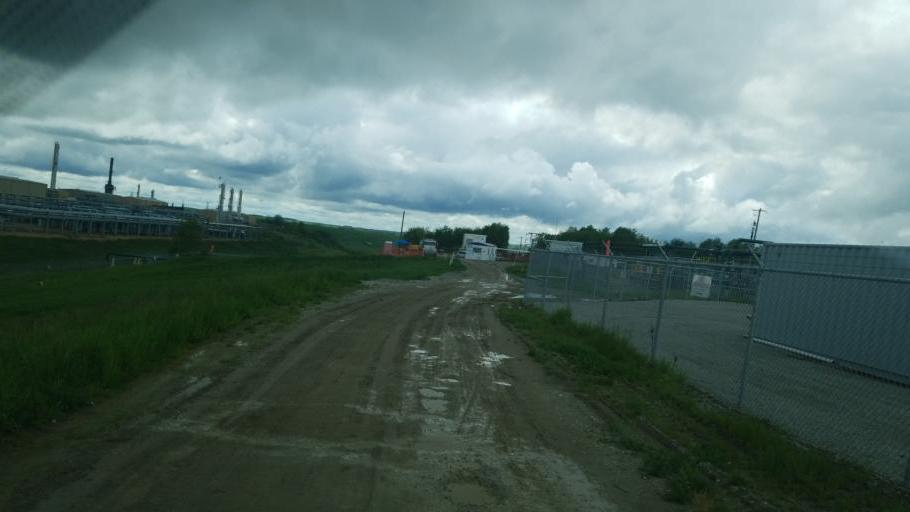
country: US
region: Ohio
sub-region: Harrison County
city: Cadiz
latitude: 40.2623
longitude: -81.0244
